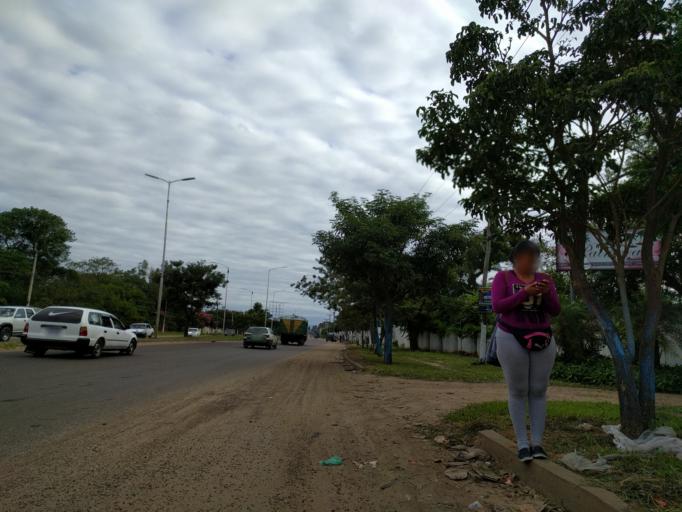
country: BO
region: Santa Cruz
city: Santa Cruz de la Sierra
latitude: -17.8529
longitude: -63.2548
